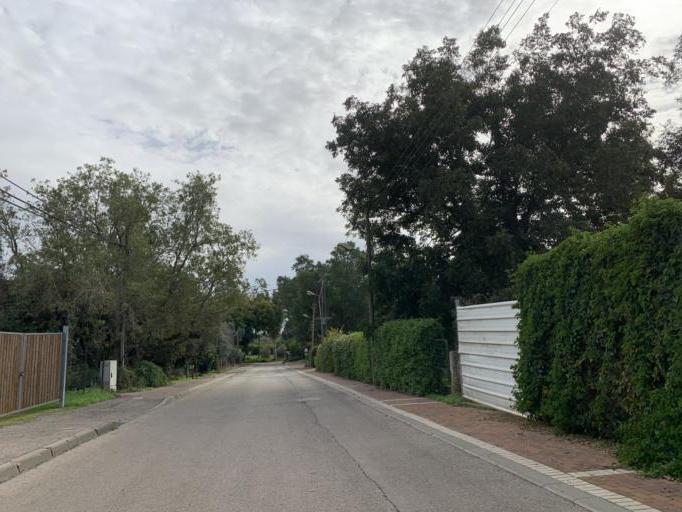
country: IL
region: Central District
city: Hod HaSharon
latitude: 32.1506
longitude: 34.8996
